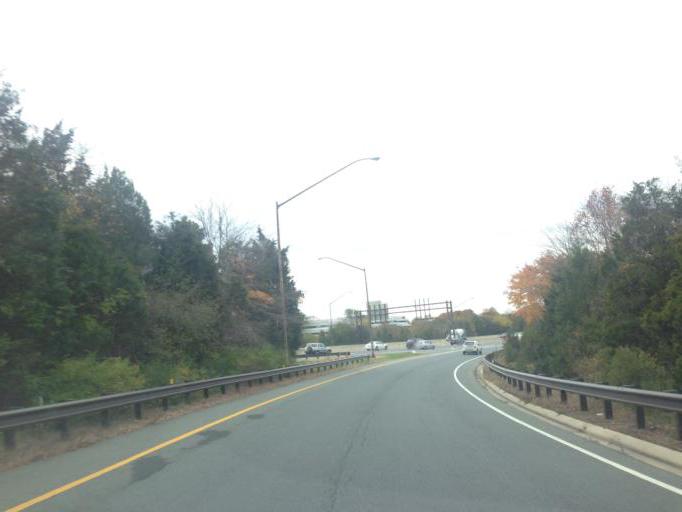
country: US
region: Maryland
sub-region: Montgomery County
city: Germantown
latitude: 39.1870
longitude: -77.2561
